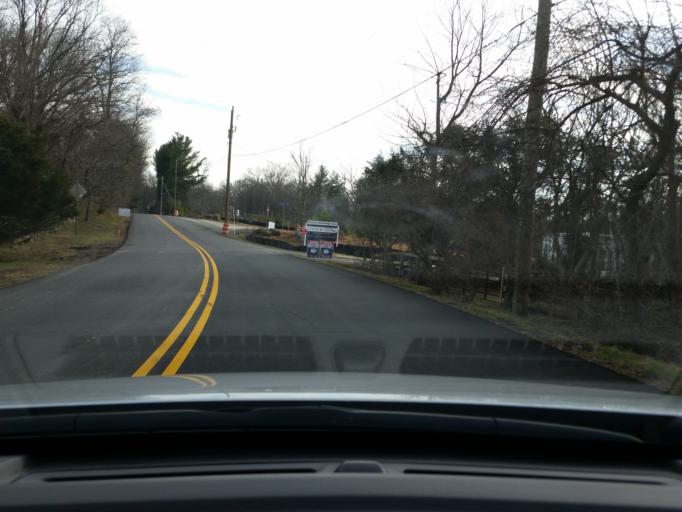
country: US
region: Virginia
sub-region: Fairfax County
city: Great Falls
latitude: 38.9905
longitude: -77.2742
